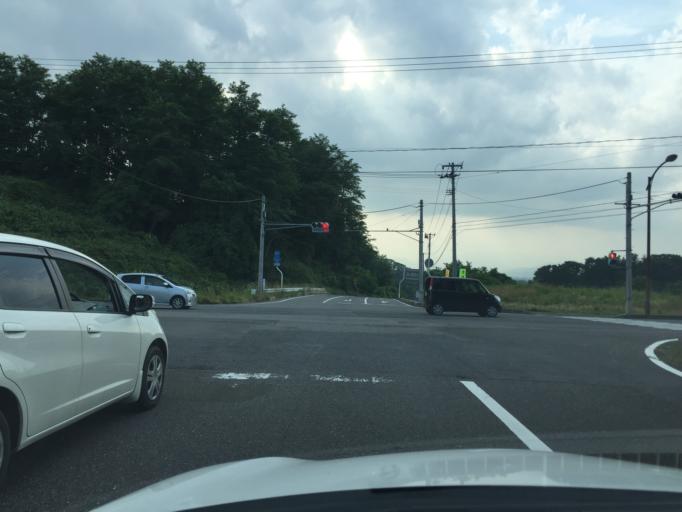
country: JP
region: Fukushima
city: Miharu
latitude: 37.3998
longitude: 140.4448
